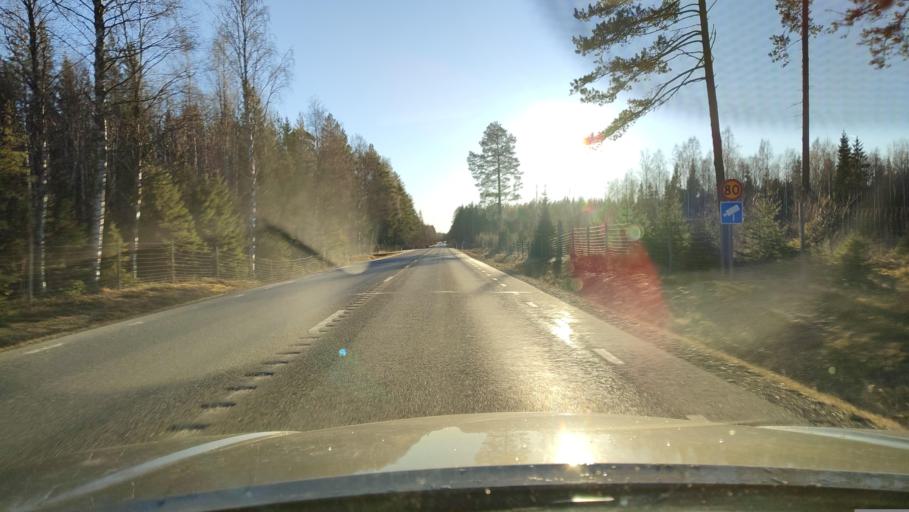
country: SE
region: Vaesterbotten
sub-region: Skelleftea Kommun
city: Burea
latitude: 64.5492
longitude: 21.2475
